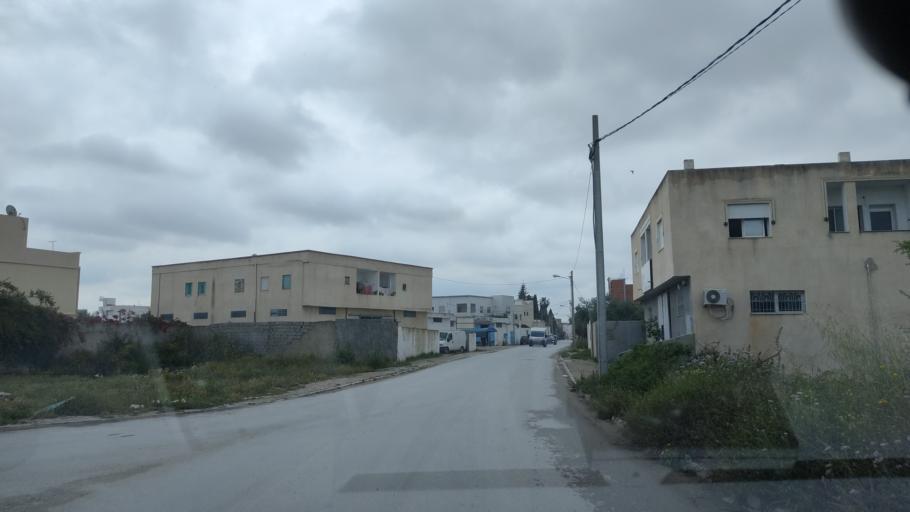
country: TN
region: Ariana
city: Ariana
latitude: 36.8813
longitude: 10.2190
